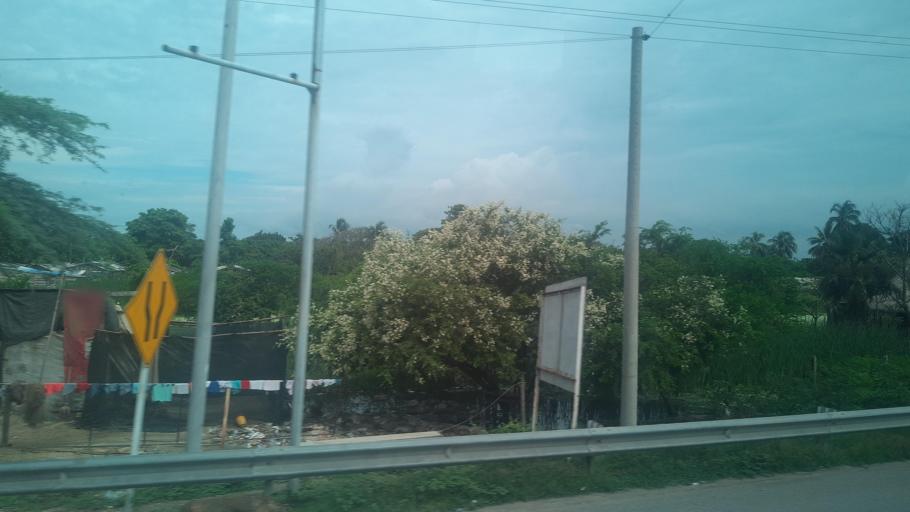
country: CO
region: Atlantico
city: Barranquilla
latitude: 10.9776
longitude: -74.7309
